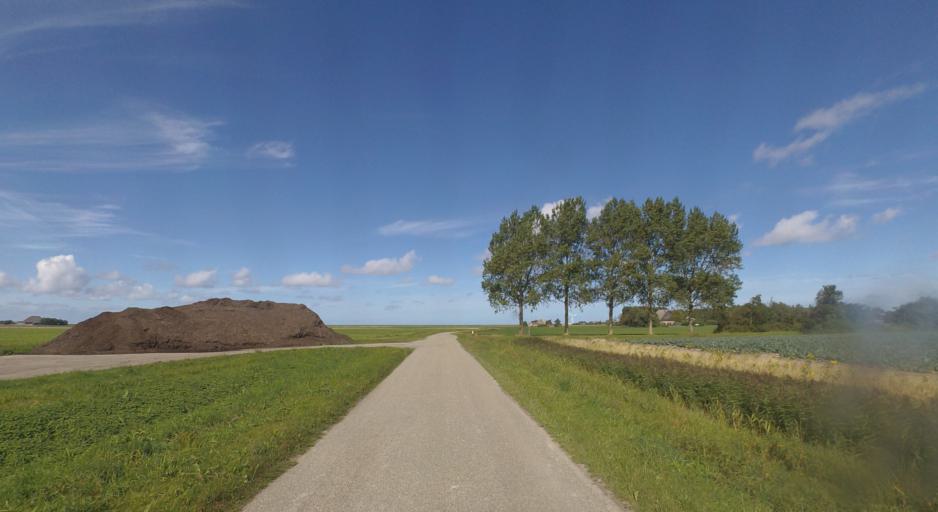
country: NL
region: Friesland
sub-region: Gemeente Dongeradeel
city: Holwerd
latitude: 53.3608
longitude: 5.8971
